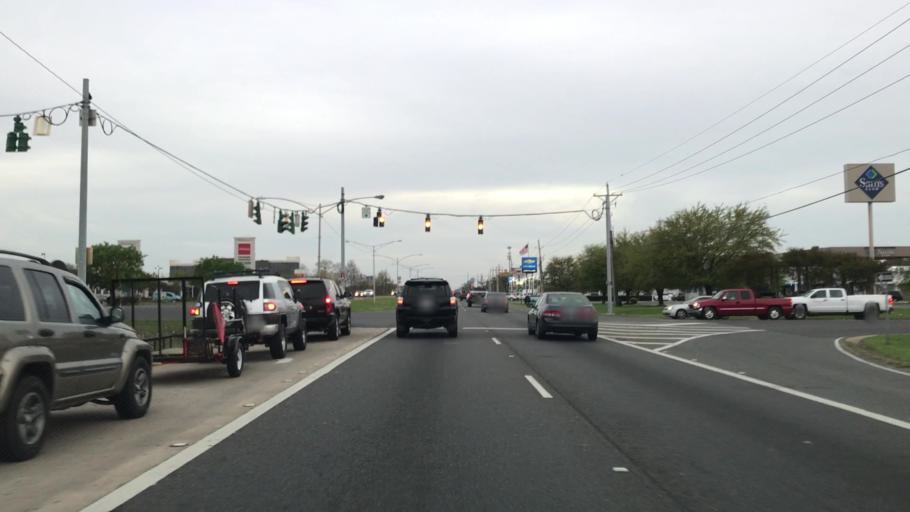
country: US
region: Louisiana
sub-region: Bossier Parish
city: Bossier City
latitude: 32.4387
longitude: -93.7160
